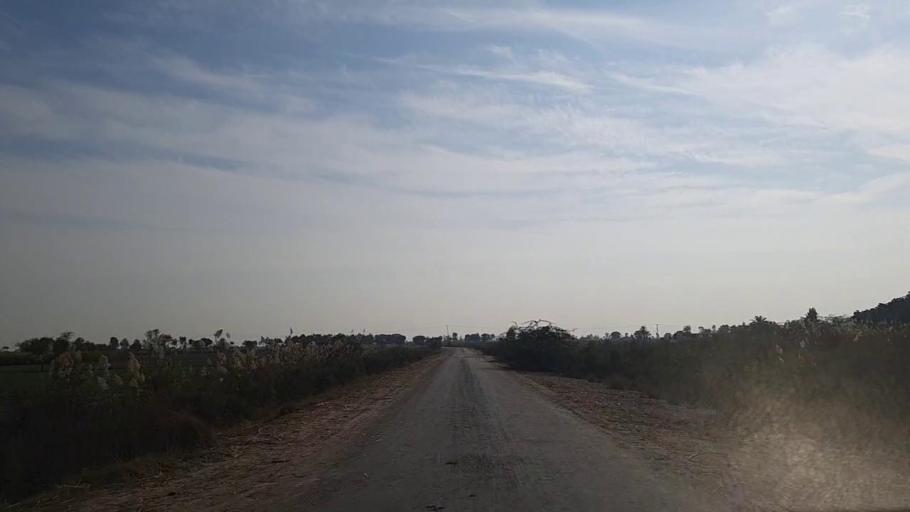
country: PK
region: Sindh
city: Daur
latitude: 26.4684
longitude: 68.4179
